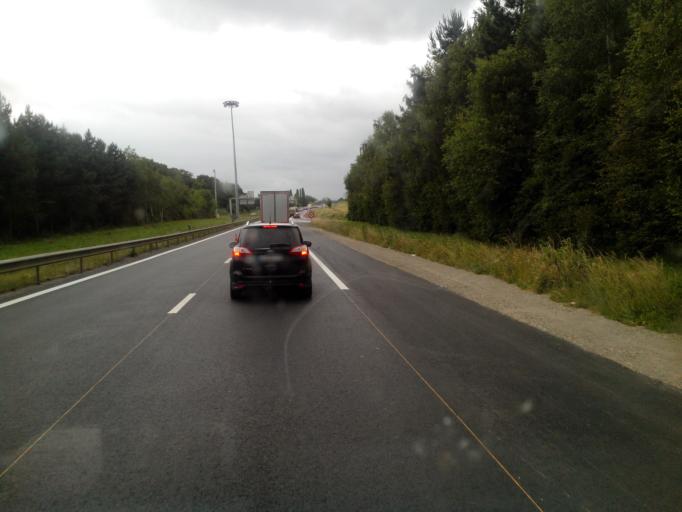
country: FR
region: Brittany
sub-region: Departement d'Ille-et-Vilaine
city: Rennes
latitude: 48.0797
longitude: -1.6751
